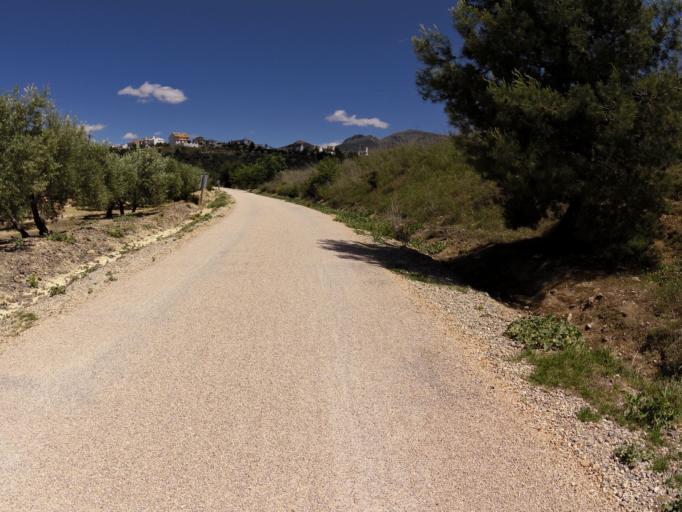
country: ES
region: Andalusia
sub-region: Provincia de Jaen
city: Torre del Campo
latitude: 37.7710
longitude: -3.9120
